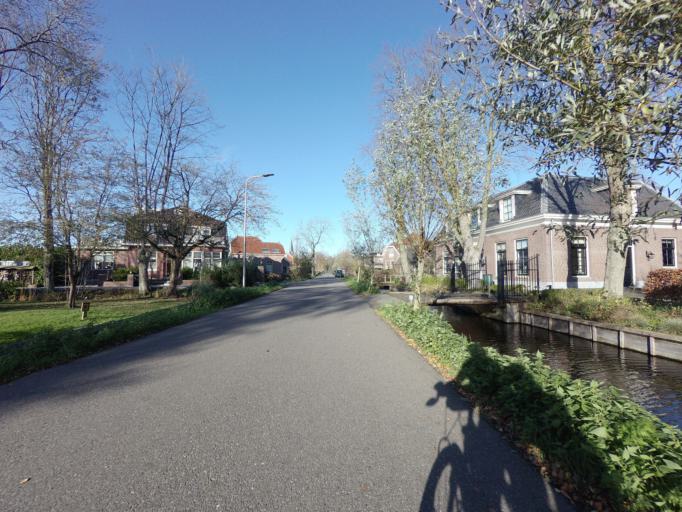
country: NL
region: South Holland
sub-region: Gemeente Nieuwkoop
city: Nieuwkoop
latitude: 52.1457
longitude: 4.7261
